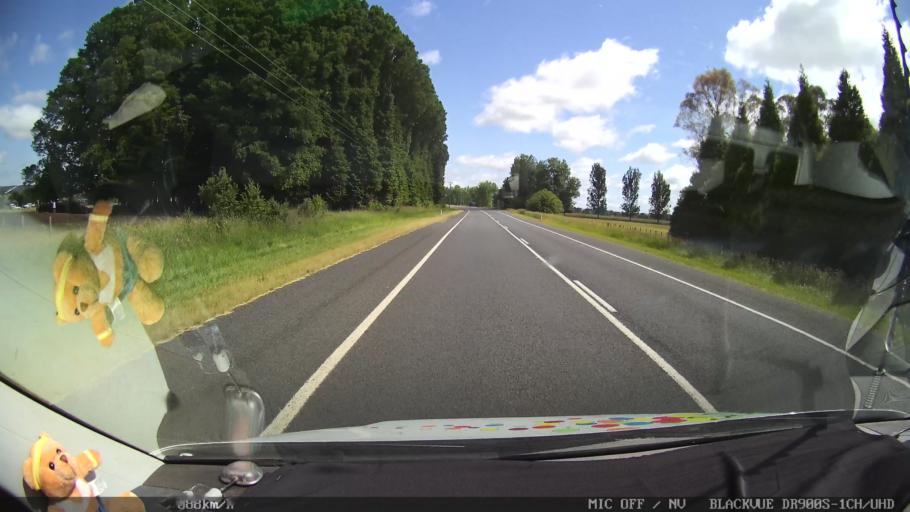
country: AU
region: New South Wales
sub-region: Glen Innes Severn
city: Glen Innes
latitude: -29.8151
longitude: 151.7412
